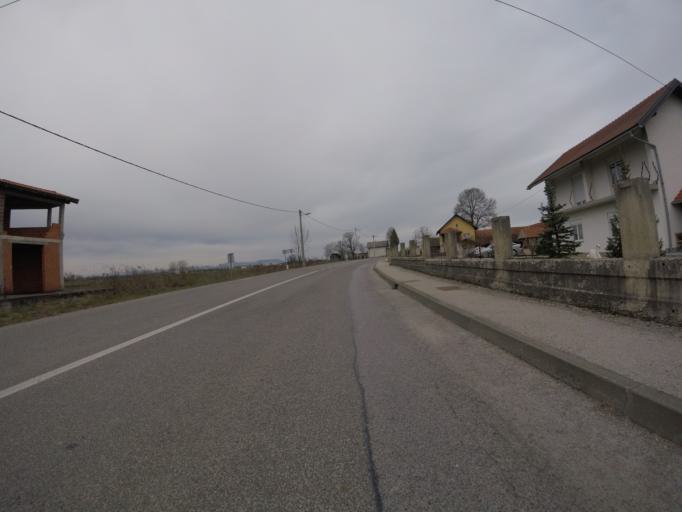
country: HR
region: Grad Zagreb
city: Horvati
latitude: 45.5784
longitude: 15.8601
